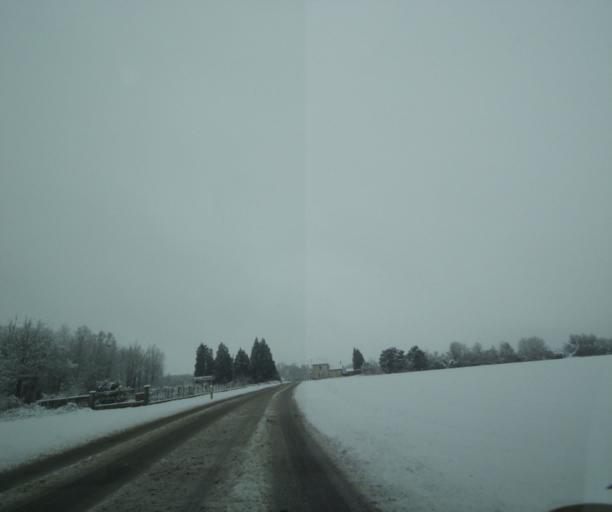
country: FR
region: Champagne-Ardenne
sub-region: Departement de la Haute-Marne
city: Saint-Dizier
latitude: 48.5898
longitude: 4.9022
